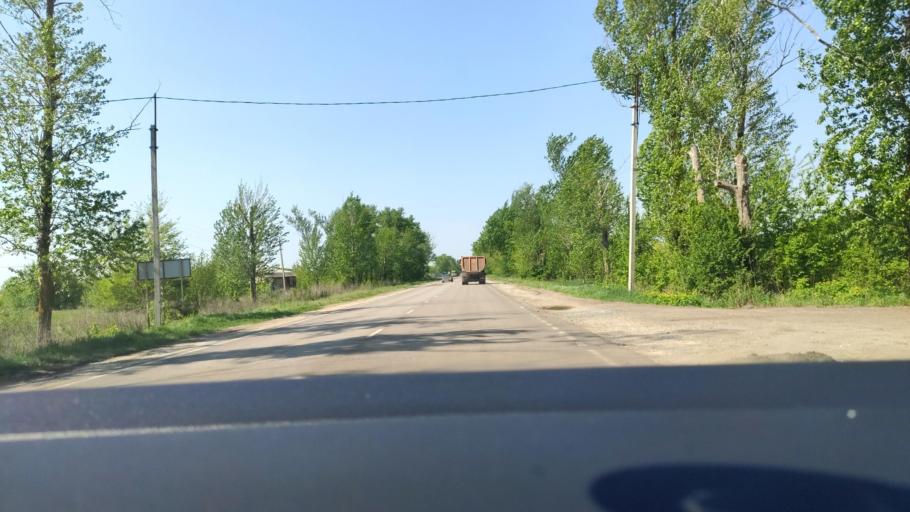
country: RU
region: Voronezj
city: Maslovka
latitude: 51.5340
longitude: 39.3216
